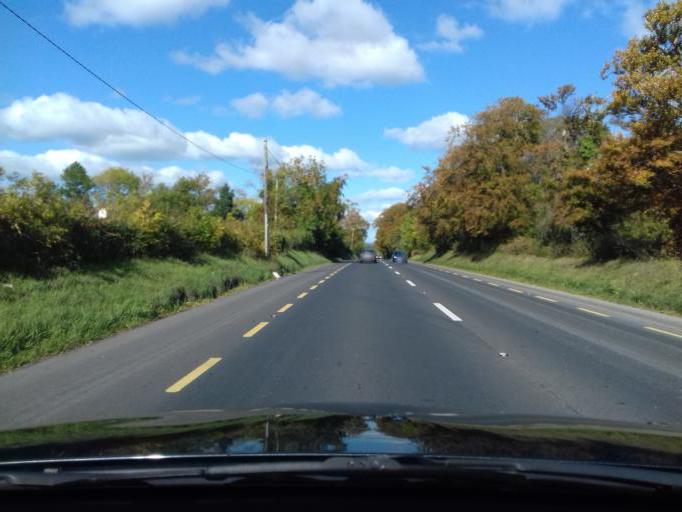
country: IE
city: Kentstown
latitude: 53.5953
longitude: -6.4665
